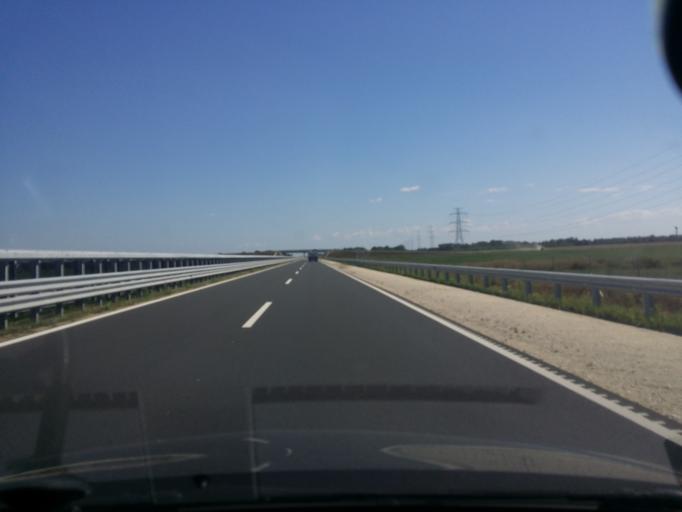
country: HU
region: Vas
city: Repcelak
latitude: 47.3773
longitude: 16.9542
